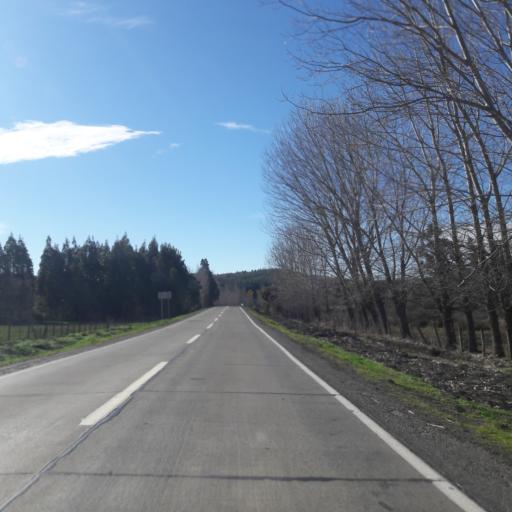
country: CL
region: Araucania
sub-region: Provincia de Malleco
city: Collipulli
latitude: -37.7838
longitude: -72.5218
